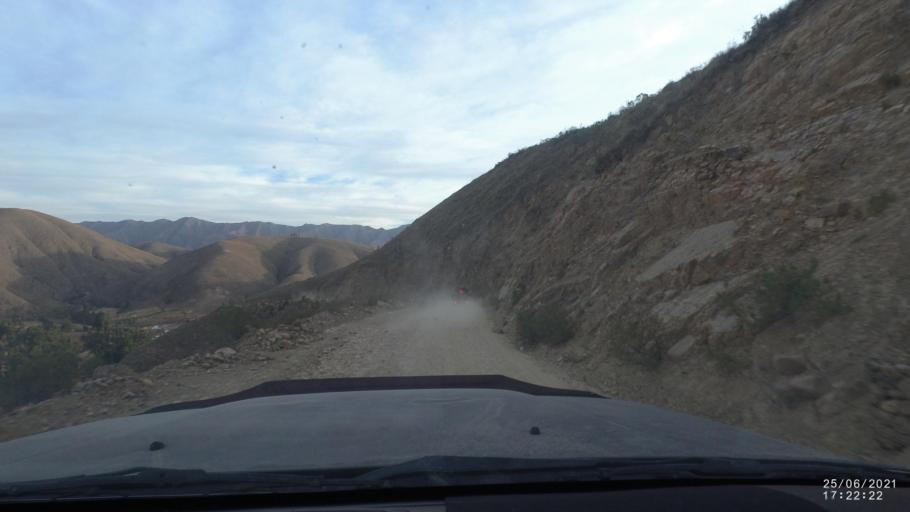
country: BO
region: Cochabamba
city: Mizque
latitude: -17.9088
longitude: -65.6847
